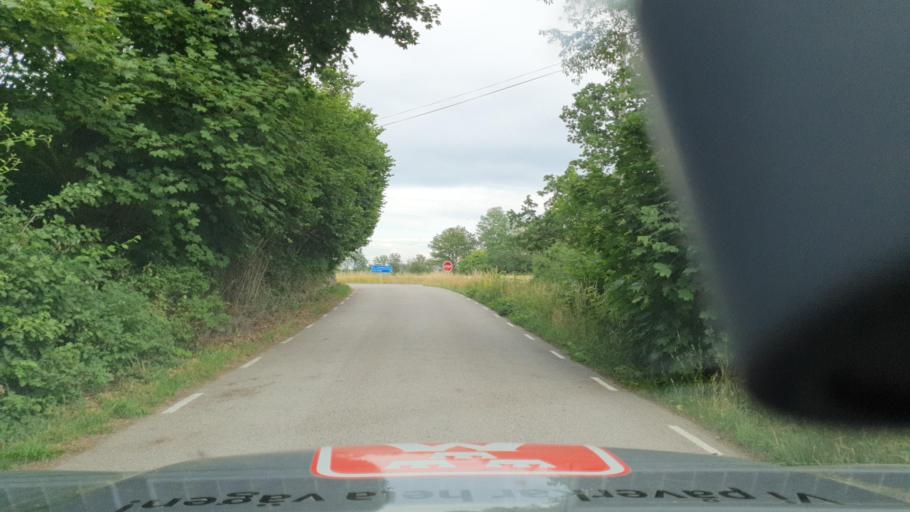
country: SE
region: Kalmar
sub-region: Kalmar Kommun
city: Ljungbyholm
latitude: 56.5862
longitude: 16.1121
